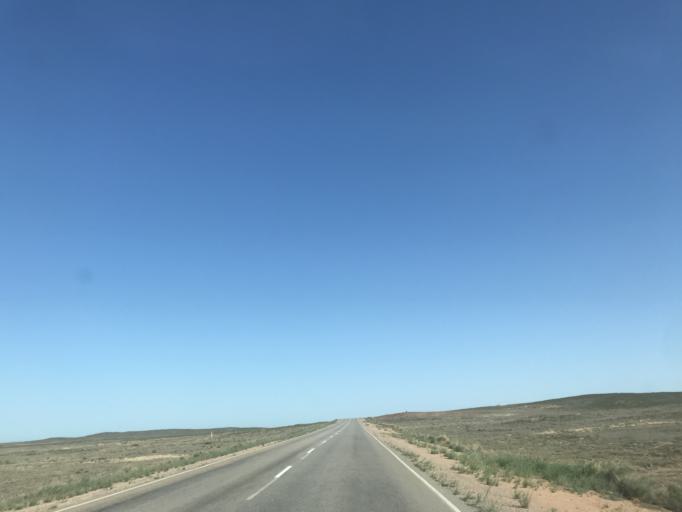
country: KZ
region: Zhambyl
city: Mynaral
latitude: 45.4926
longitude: 73.5264
